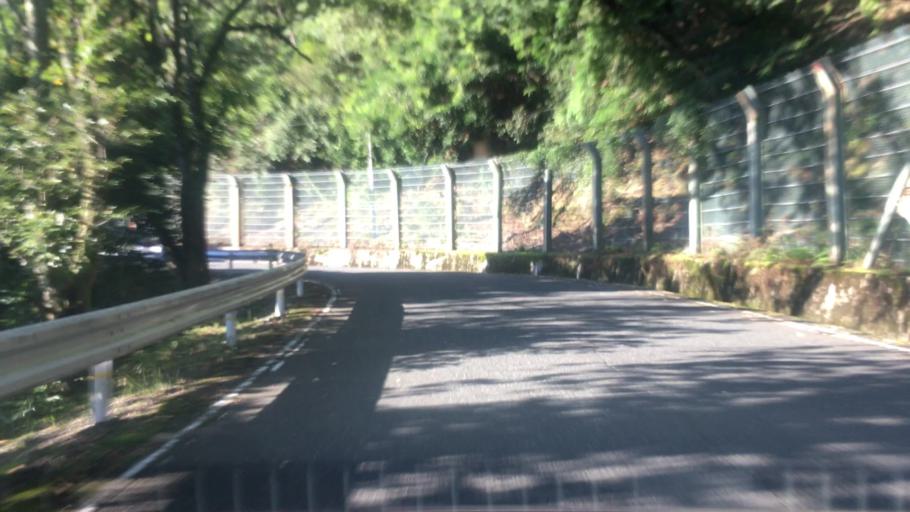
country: JP
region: Hyogo
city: Toyooka
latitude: 35.6159
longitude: 134.8751
